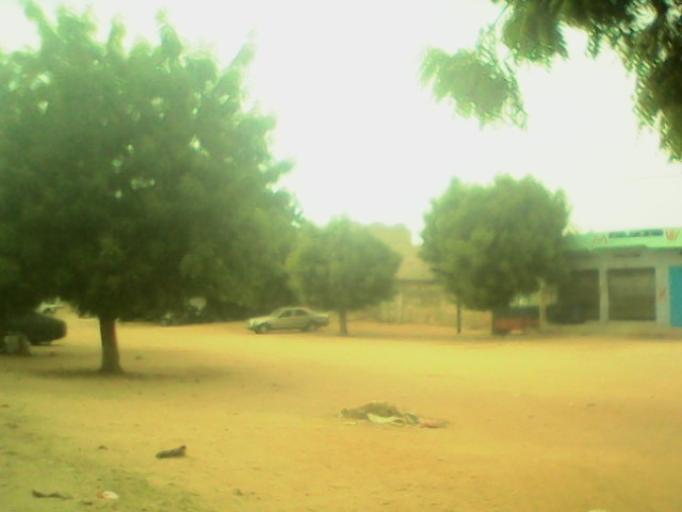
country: SN
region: Diourbel
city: Touba
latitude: 14.8824
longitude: -15.8865
